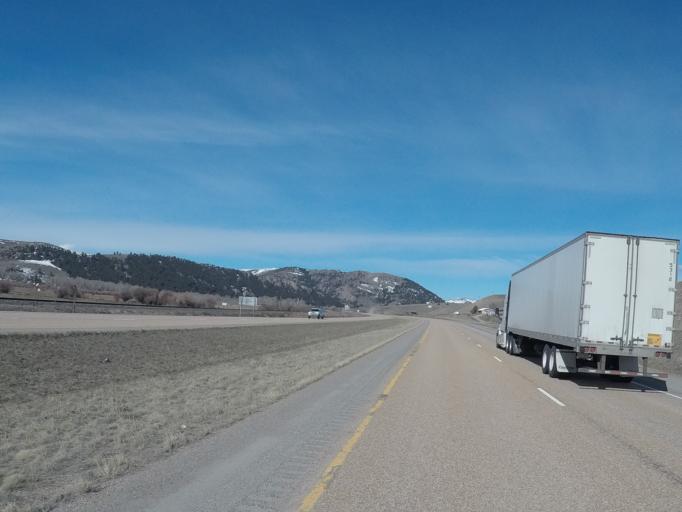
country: US
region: Montana
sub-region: Granite County
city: Philipsburg
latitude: 46.6760
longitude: -113.1692
